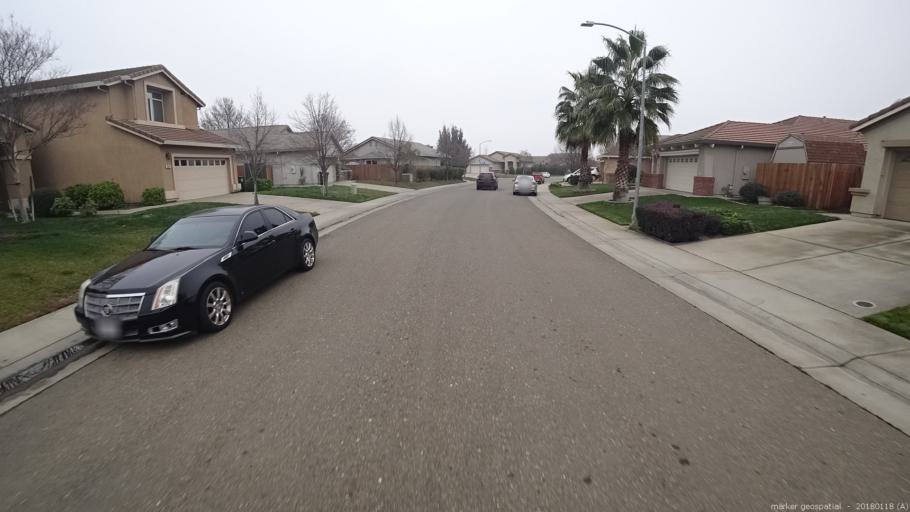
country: US
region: California
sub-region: Sacramento County
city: Rancho Cordova
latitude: 38.5790
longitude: -121.2869
